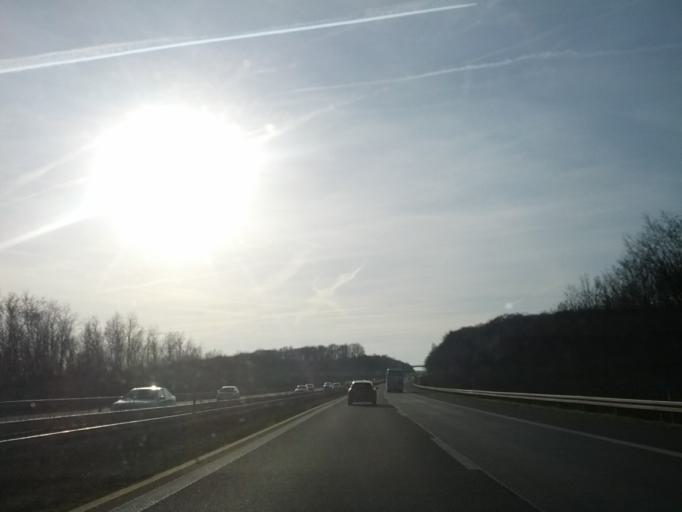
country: DE
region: Bavaria
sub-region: Regierungsbezirk Unterfranken
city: Unterpleichfeld
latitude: 49.8908
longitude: 10.0002
